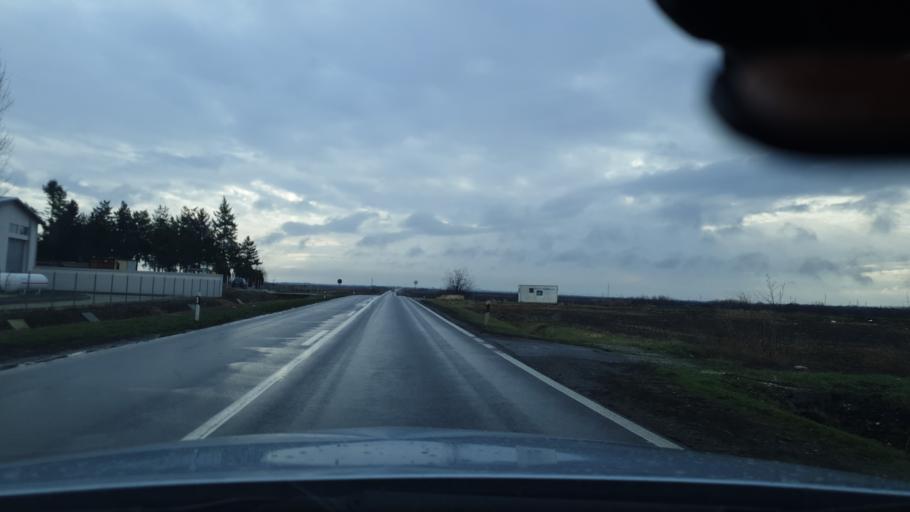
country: RS
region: Autonomna Pokrajina Vojvodina
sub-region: Juznobanatski Okrug
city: Kovin
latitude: 44.8055
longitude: 20.8958
